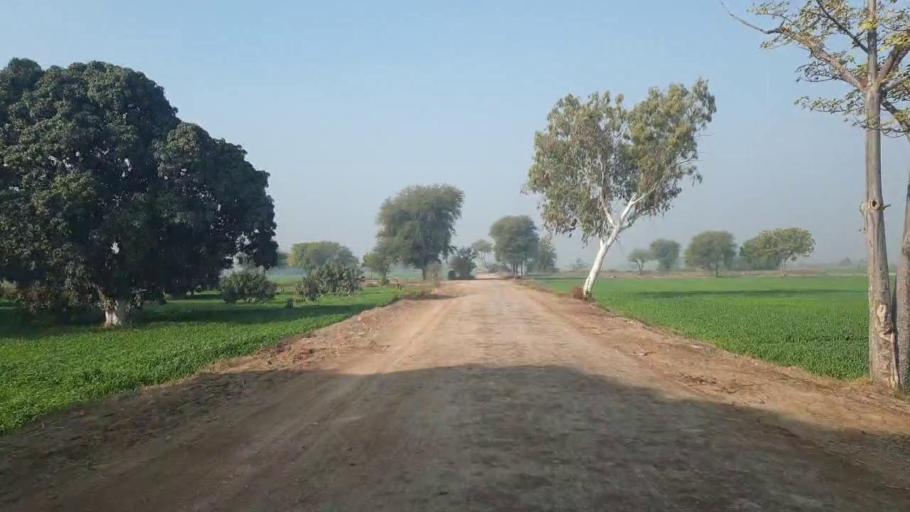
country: PK
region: Sindh
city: Shahdadpur
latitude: 25.9437
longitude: 68.5903
